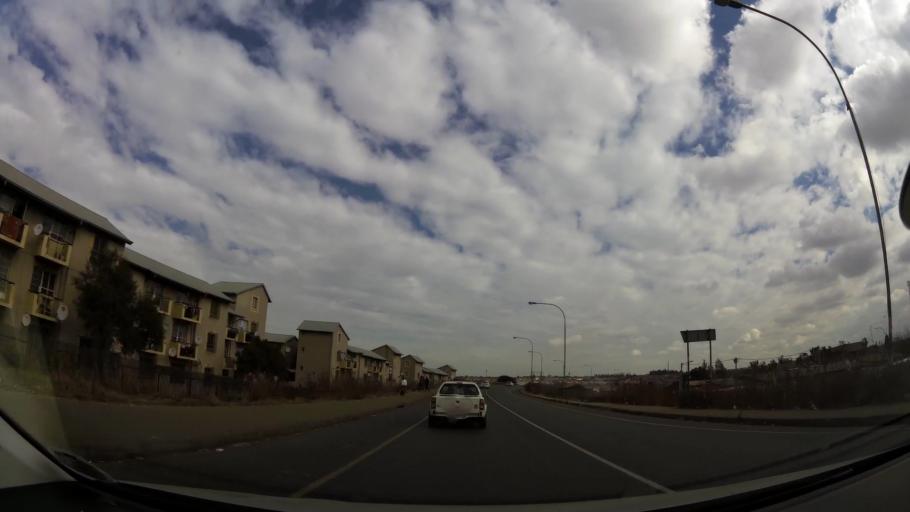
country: ZA
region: Gauteng
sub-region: City of Johannesburg Metropolitan Municipality
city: Soweto
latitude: -26.2746
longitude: 27.8894
